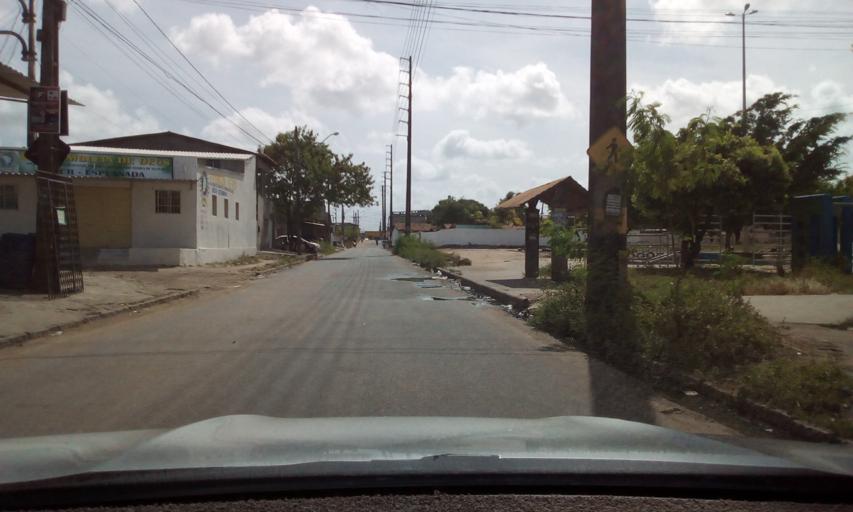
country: BR
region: Paraiba
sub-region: Joao Pessoa
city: Joao Pessoa
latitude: -7.1733
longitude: -34.8875
